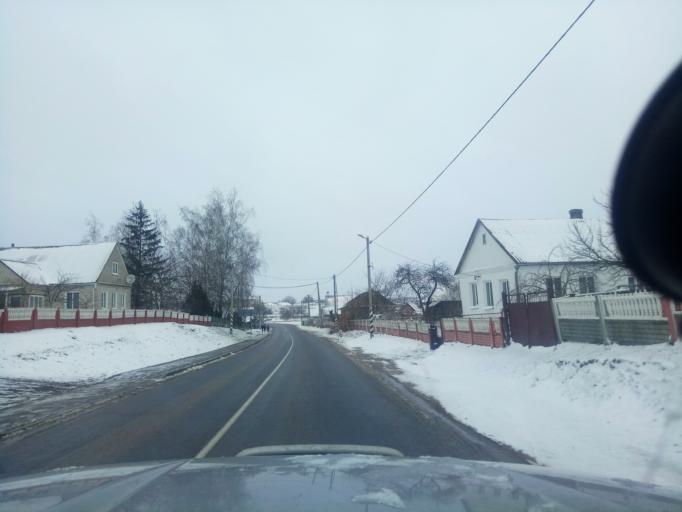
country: BY
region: Minsk
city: Tsimkavichy
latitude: 53.0674
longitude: 26.9877
